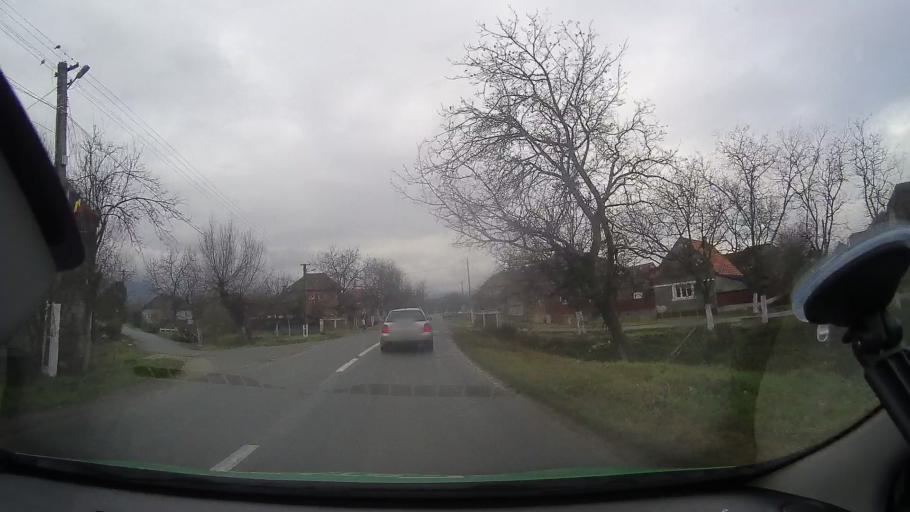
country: RO
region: Arad
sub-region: Comuna Buteni
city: Buteni
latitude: 46.3320
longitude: 22.1258
